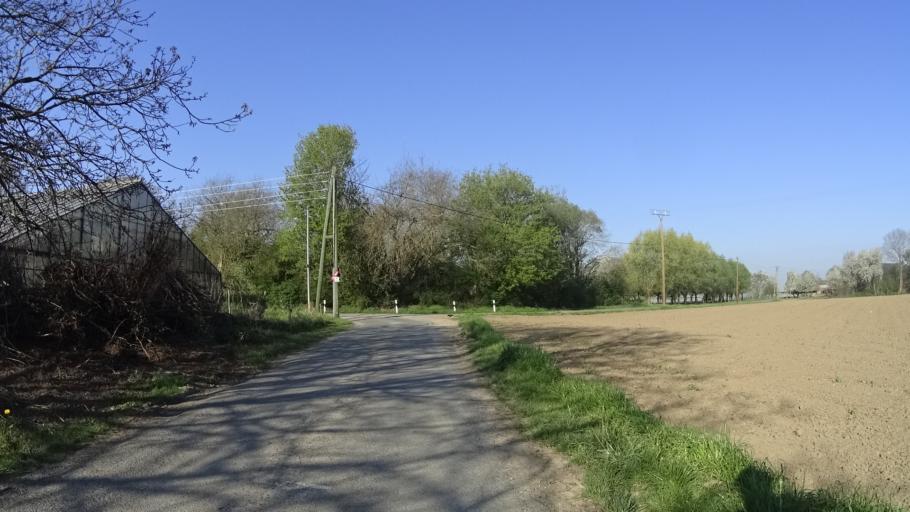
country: DE
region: North Rhine-Westphalia
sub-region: Regierungsbezirk Dusseldorf
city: Wesel
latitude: 51.6410
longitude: 6.5819
